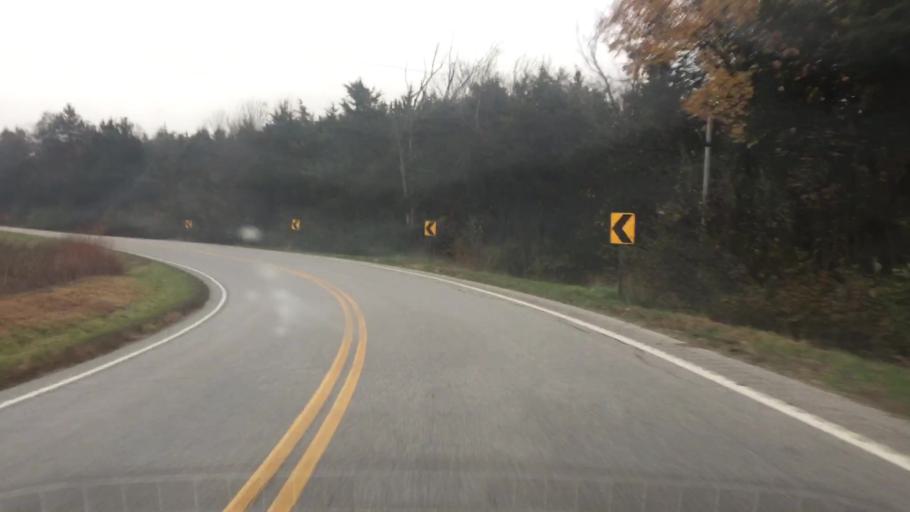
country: US
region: Missouri
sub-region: Callaway County
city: Fulton
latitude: 38.8762
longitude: -92.0788
